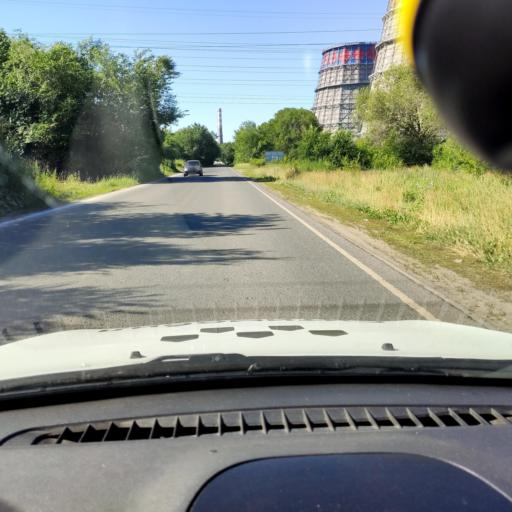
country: RU
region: Samara
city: Tol'yatti
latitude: 53.5782
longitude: 49.2553
